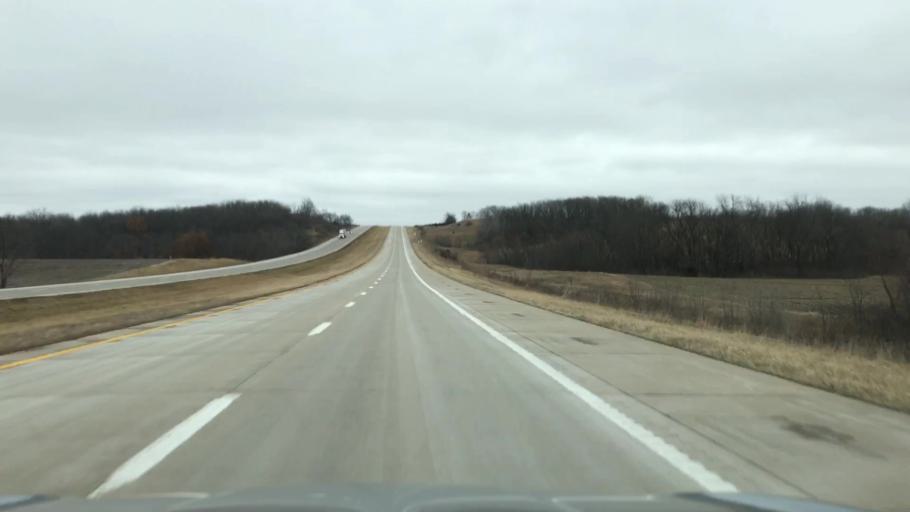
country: US
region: Missouri
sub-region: Livingston County
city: Chillicothe
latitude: 39.7353
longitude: -93.7555
